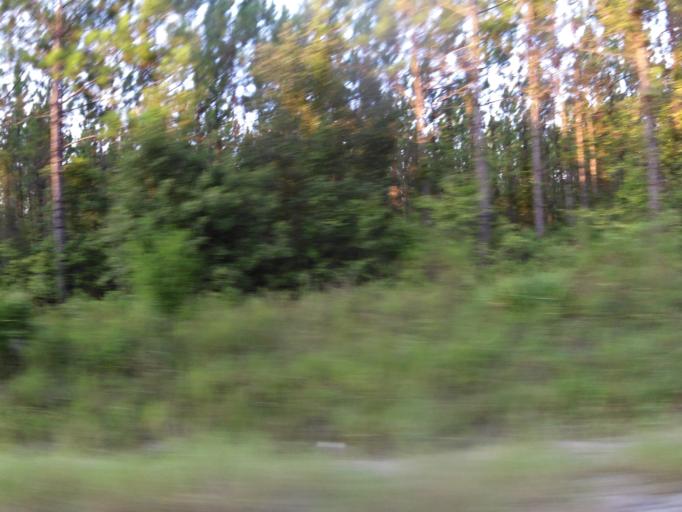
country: US
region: Florida
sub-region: Duval County
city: Baldwin
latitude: 30.3874
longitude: -82.0486
